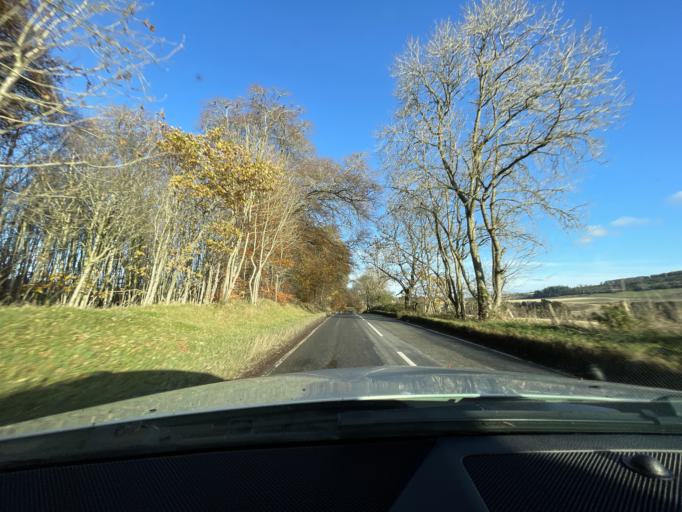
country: GB
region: Scotland
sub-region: Highland
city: Inverness
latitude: 57.4260
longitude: -4.2882
